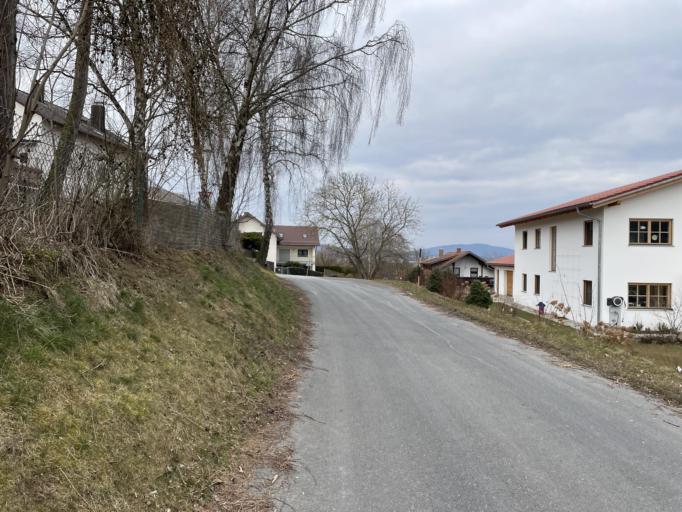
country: DE
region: Bavaria
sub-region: Upper Palatinate
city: Runding
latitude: 49.2199
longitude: 12.7654
